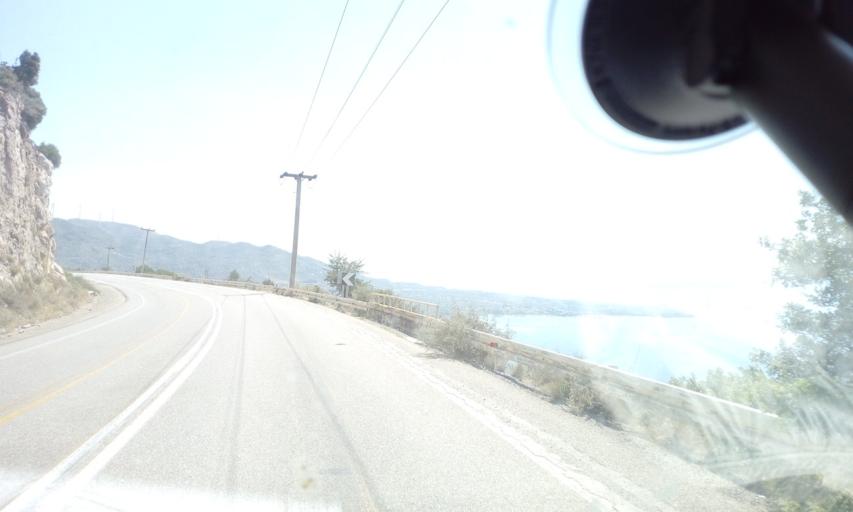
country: GR
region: West Greece
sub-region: Nomos Aitolias kai Akarnanias
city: Antirrio
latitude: 38.3485
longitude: 21.6897
